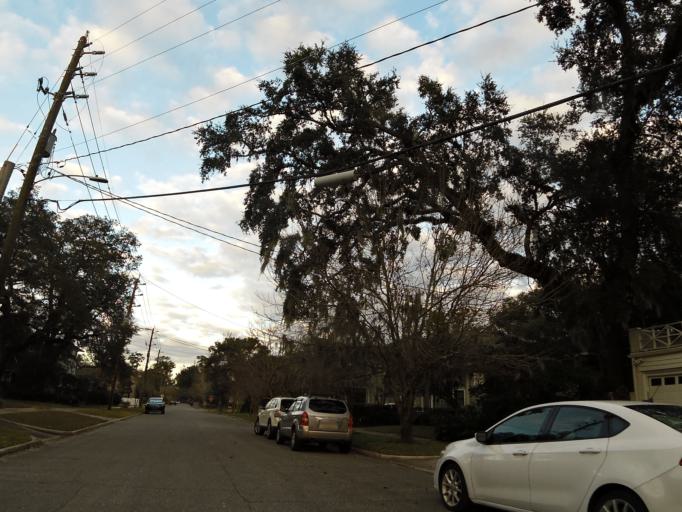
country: US
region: Florida
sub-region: Duval County
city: Jacksonville
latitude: 30.2929
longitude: -81.7067
